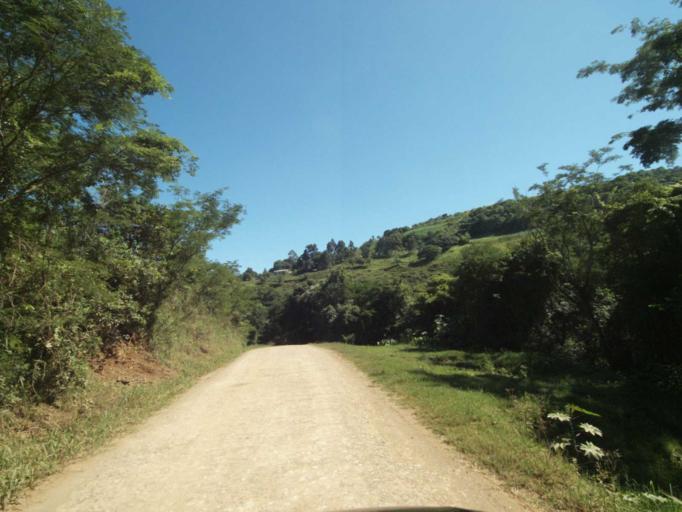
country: BR
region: Parana
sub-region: Francisco Beltrao
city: Francisco Beltrao
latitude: -26.1480
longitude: -53.3041
